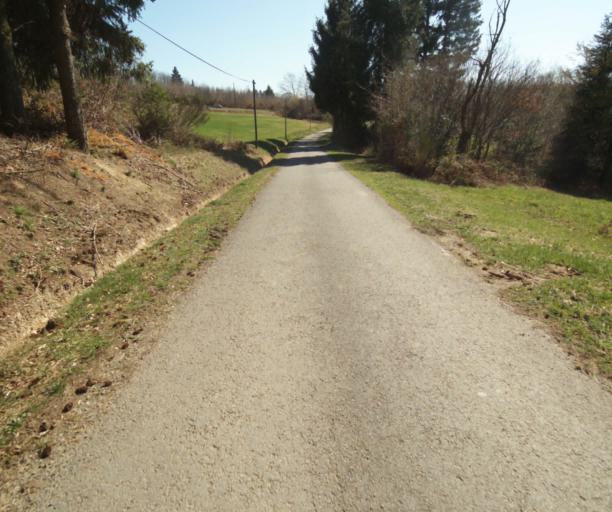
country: FR
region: Limousin
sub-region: Departement de la Correze
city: Saint-Mexant
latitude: 45.3006
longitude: 1.6715
